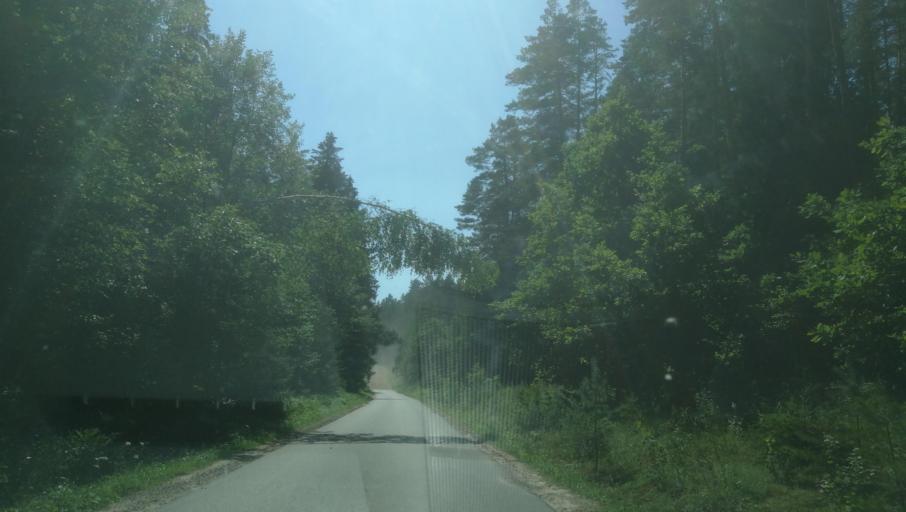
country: LV
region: Cesu Rajons
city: Cesis
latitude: 57.2839
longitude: 25.2126
